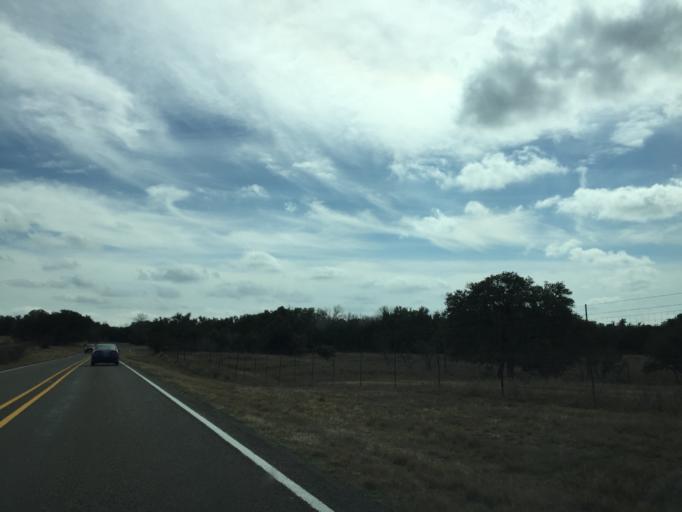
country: US
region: Texas
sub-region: Burnet County
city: Granite Shoals
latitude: 30.5123
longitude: -98.4413
